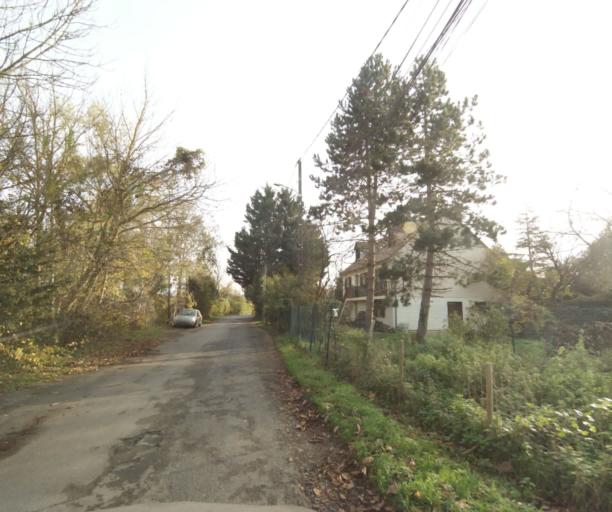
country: FR
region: Ile-de-France
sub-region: Departement du Val-d'Oise
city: Herblay
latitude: 48.9821
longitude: 2.1587
